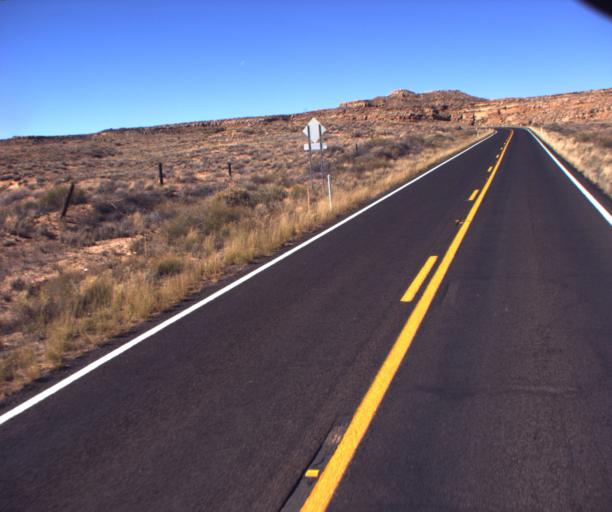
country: US
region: Arizona
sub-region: Navajo County
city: First Mesa
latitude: 35.8820
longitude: -110.6168
